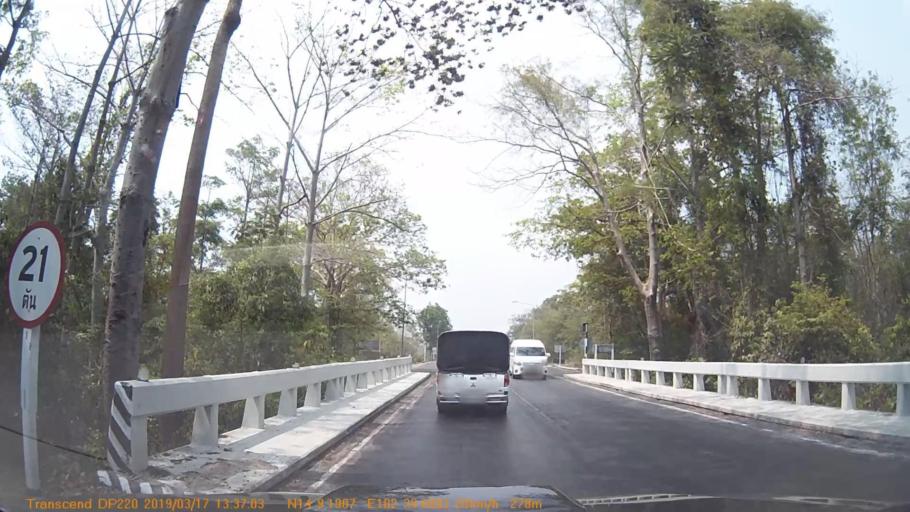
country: TH
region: Buriram
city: Non Din Daeng
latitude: 14.1532
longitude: 102.6614
